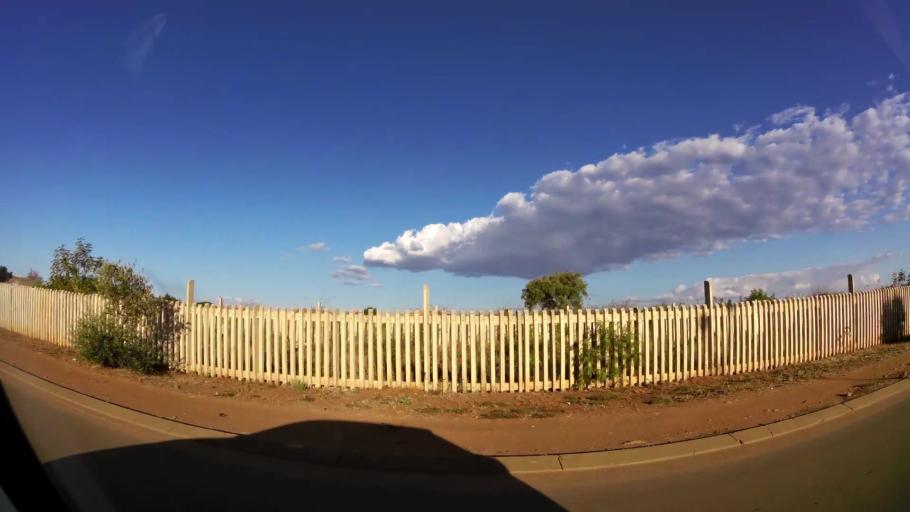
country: ZA
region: Limpopo
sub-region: Waterberg District Municipality
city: Mokopane
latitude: -24.1444
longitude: 28.9902
